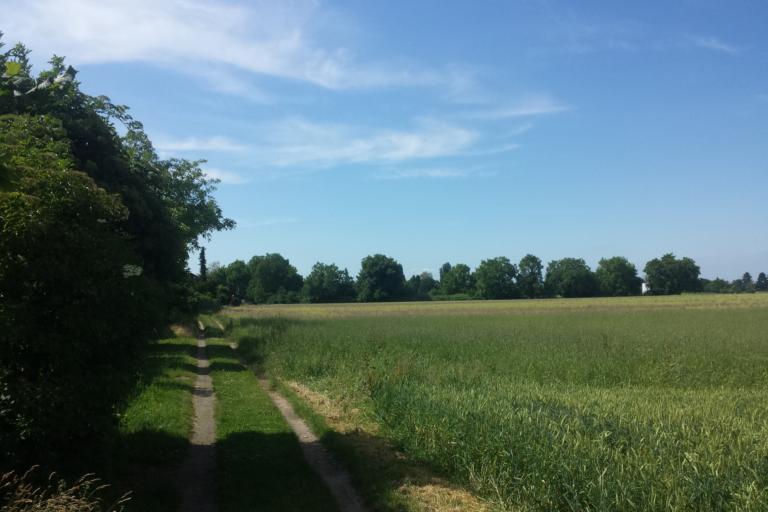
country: DE
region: Baden-Wuerttemberg
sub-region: Karlsruhe Region
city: Edingen-Neckarhausen
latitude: 49.4442
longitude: 8.5889
